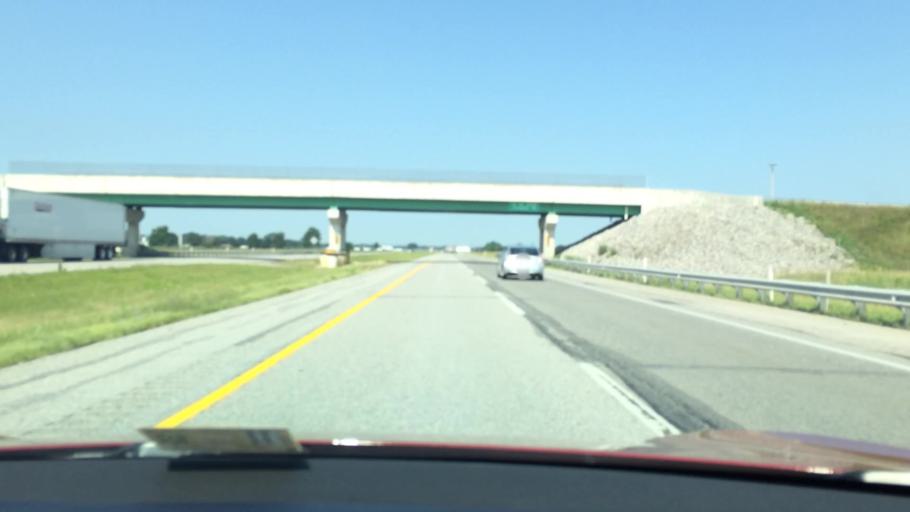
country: US
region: Michigan
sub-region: Saint Joseph County
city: Sturgis
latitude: 41.7457
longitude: -85.5140
